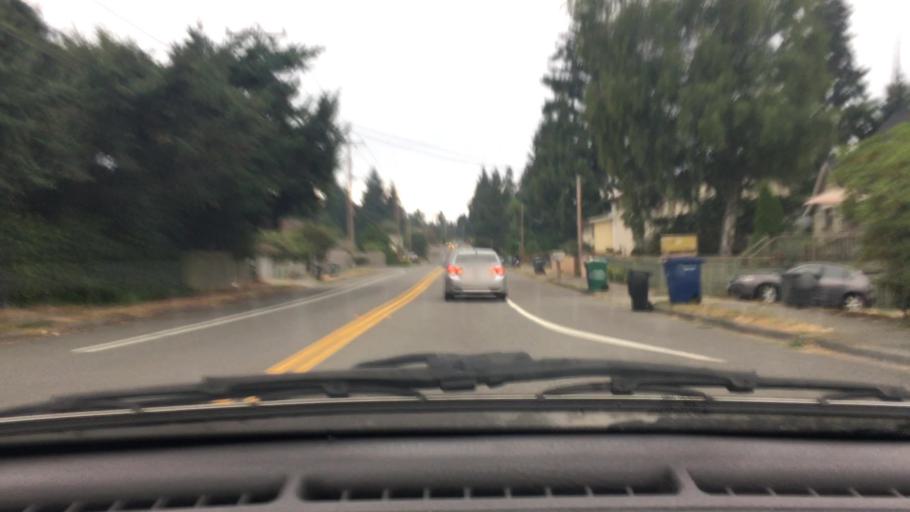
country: US
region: Washington
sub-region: King County
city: Burien
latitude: 47.4596
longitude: -122.3500
